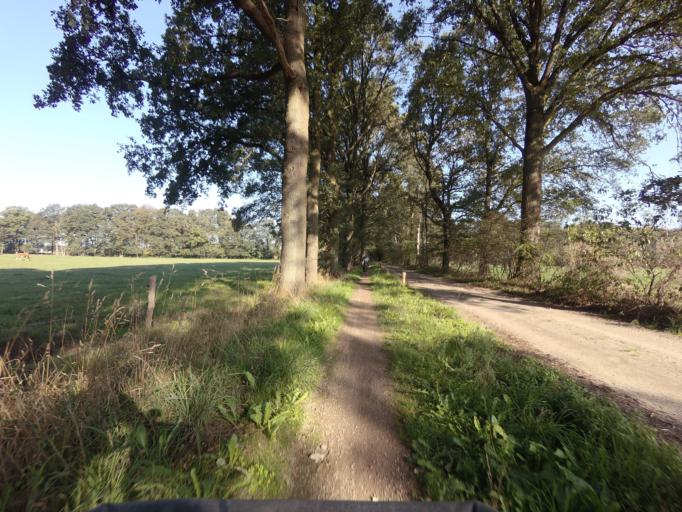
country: NL
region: Overijssel
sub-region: Gemeente Raalte
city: Raalte
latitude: 52.3197
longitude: 6.2858
